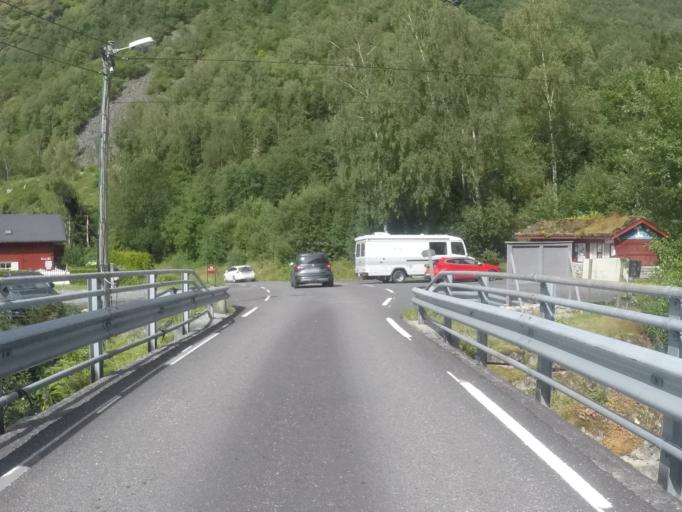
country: NO
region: Sogn og Fjordane
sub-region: Stryn
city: Stryn
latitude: 61.8011
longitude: 7.0113
